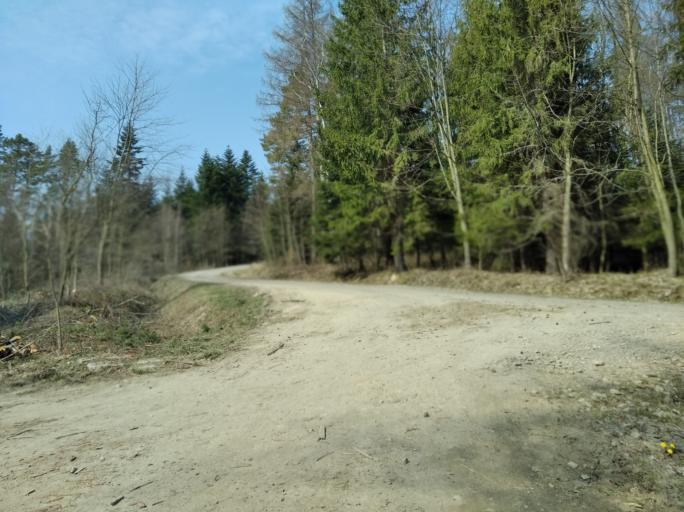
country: PL
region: Subcarpathian Voivodeship
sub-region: Powiat strzyzowski
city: Wysoka Strzyzowska
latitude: 49.8122
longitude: 21.7885
